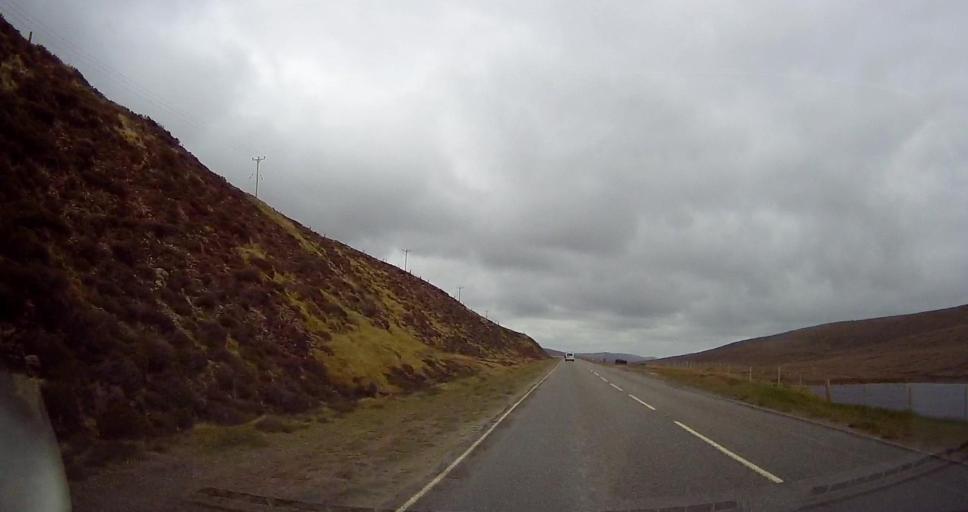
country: GB
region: Scotland
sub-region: Shetland Islands
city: Lerwick
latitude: 60.3155
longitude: -1.2467
